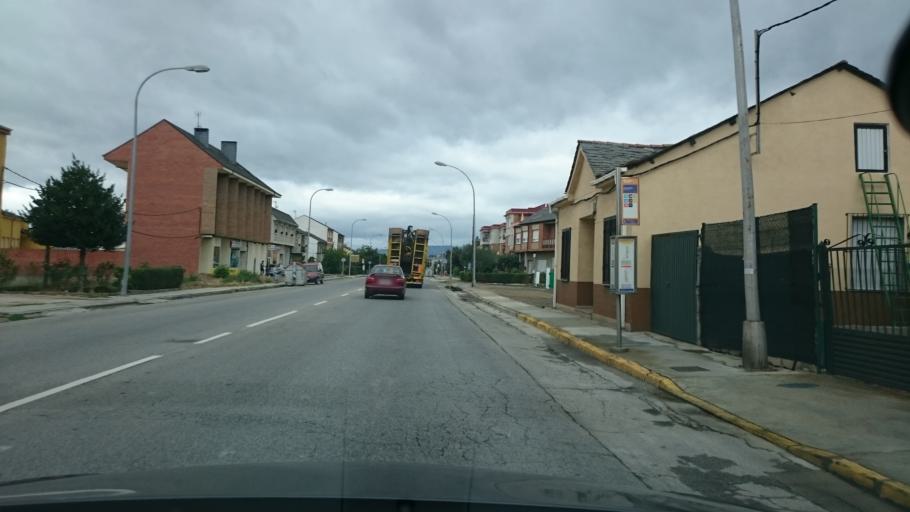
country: ES
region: Castille and Leon
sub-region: Provincia de Leon
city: Camponaraya
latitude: 42.5636
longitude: -6.6327
